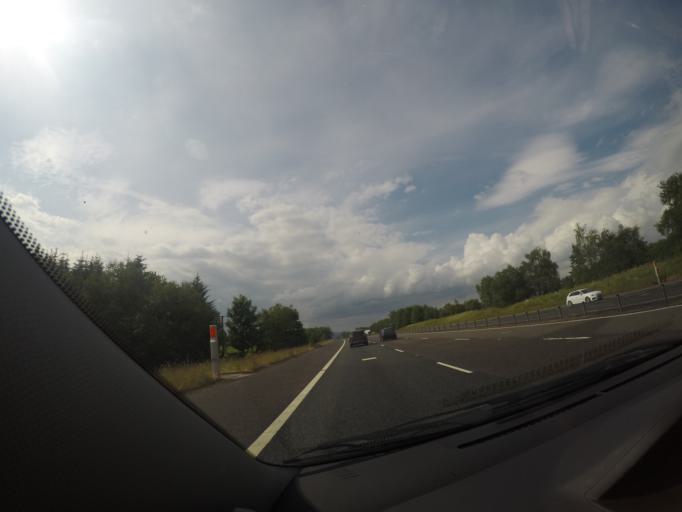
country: GB
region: Scotland
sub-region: Dumfries and Galloway
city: Lockerbie
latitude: 55.1716
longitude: -3.3946
